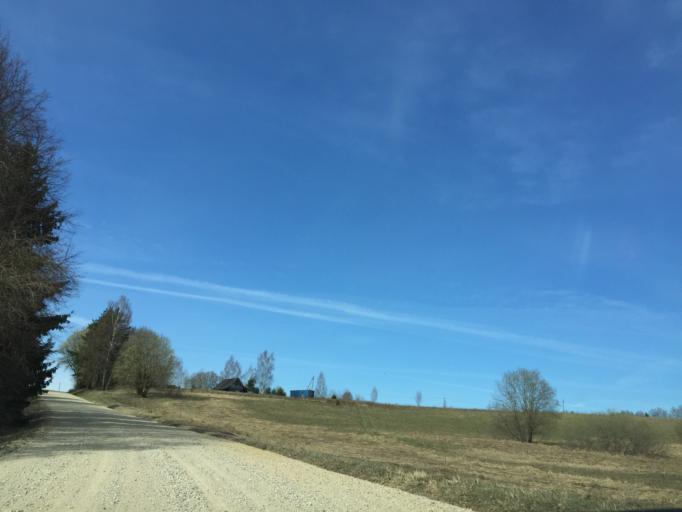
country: EE
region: Vorumaa
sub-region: Antsla vald
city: Vana-Antsla
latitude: 57.9476
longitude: 26.3749
